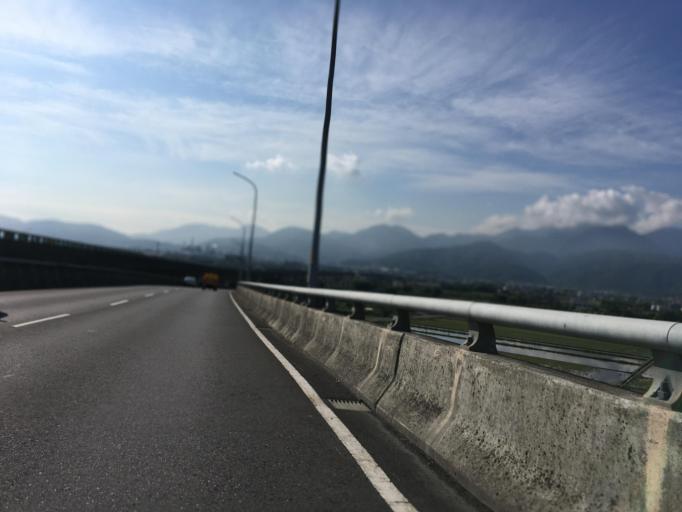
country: TW
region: Taiwan
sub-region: Yilan
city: Yilan
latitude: 24.6571
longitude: 121.8029
